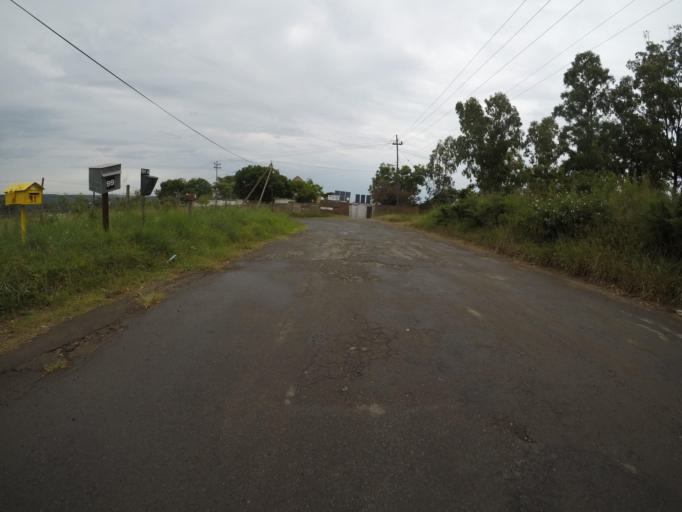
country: ZA
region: Eastern Cape
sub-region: Buffalo City Metropolitan Municipality
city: East London
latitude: -32.9611
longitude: 27.8407
